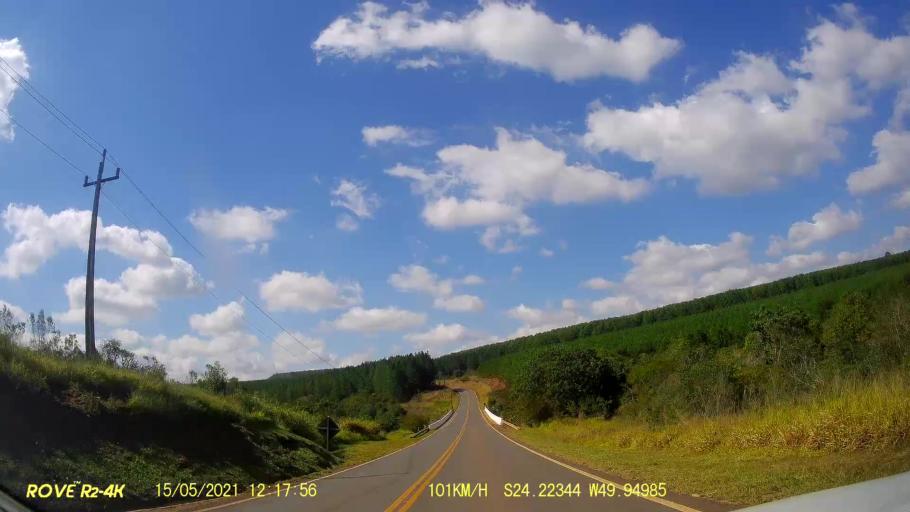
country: BR
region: Parana
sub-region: Jaguariaiva
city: Jaguariaiva
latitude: -24.2226
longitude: -49.9508
